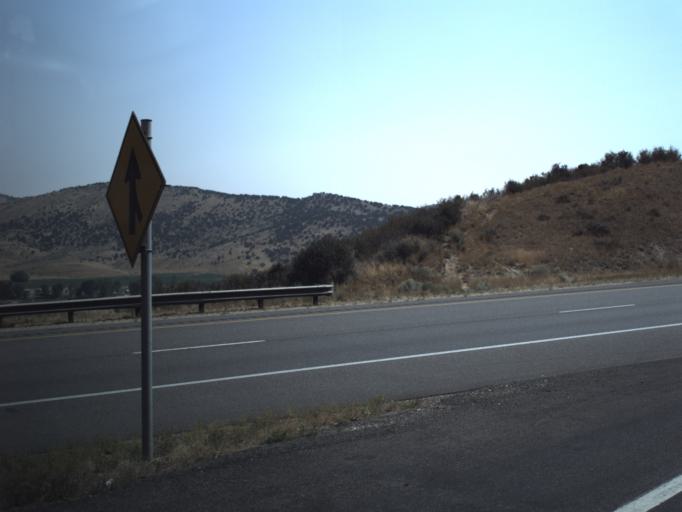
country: US
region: Utah
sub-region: Summit County
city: Coalville
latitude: 40.9381
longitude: -111.4104
